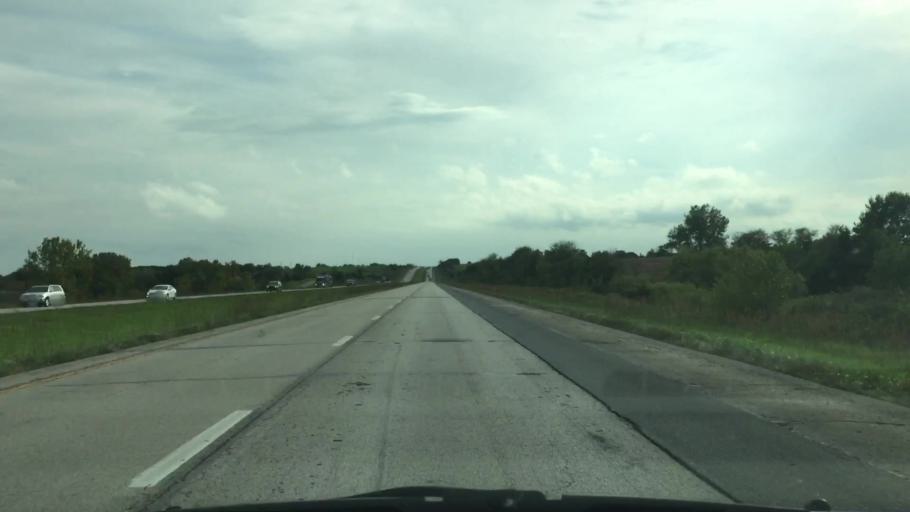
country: US
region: Iowa
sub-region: Decatur County
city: Lamoni
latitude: 40.5123
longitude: -93.9642
